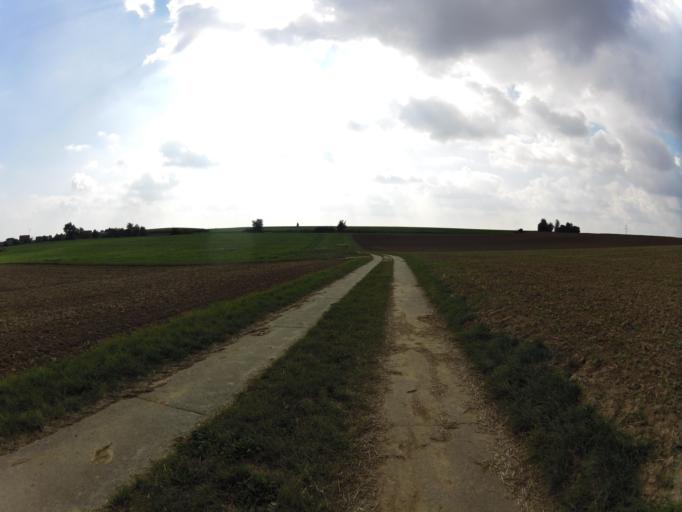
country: DE
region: Bavaria
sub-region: Regierungsbezirk Unterfranken
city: Prosselsheim
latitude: 49.8653
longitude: 10.1180
